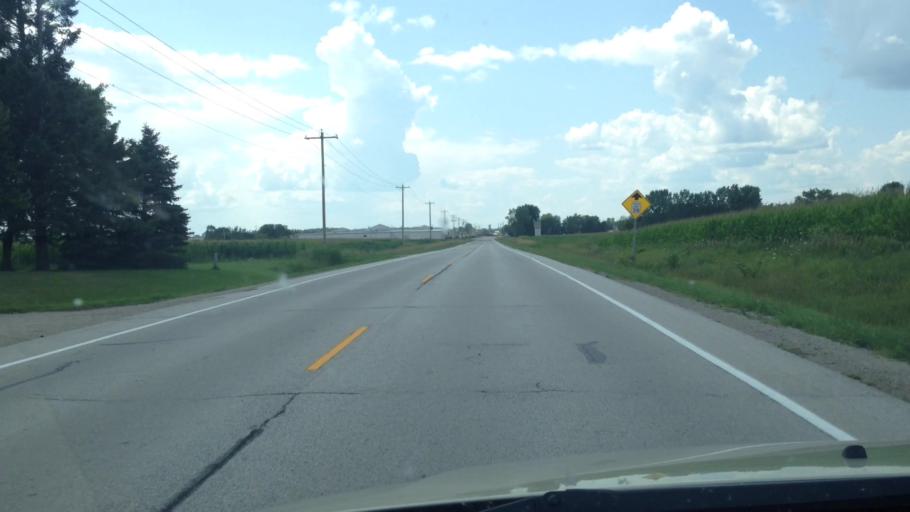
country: US
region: Wisconsin
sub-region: Brown County
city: Pulaski
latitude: 44.6576
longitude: -88.2116
